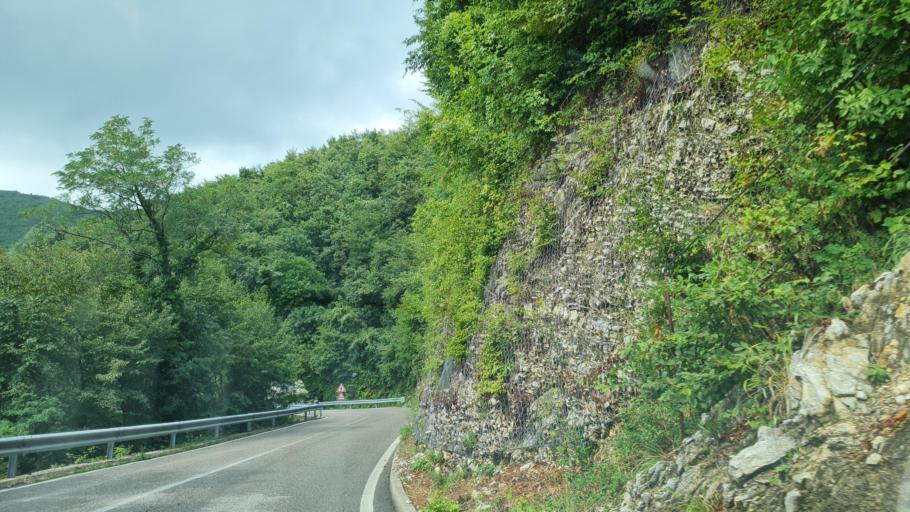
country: IT
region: Veneto
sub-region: Provincia di Vicenza
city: Marostica
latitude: 45.7881
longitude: 11.6581
